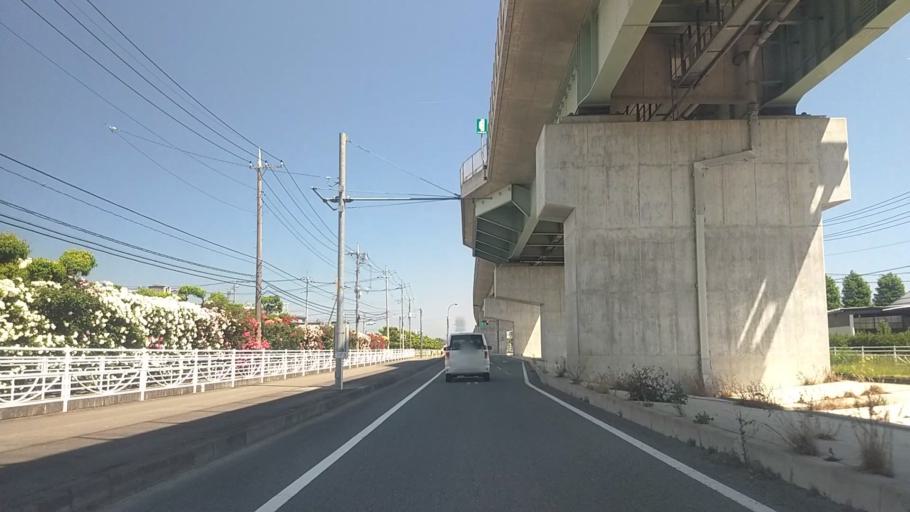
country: JP
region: Yamanashi
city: Ryuo
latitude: 35.5803
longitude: 138.4751
